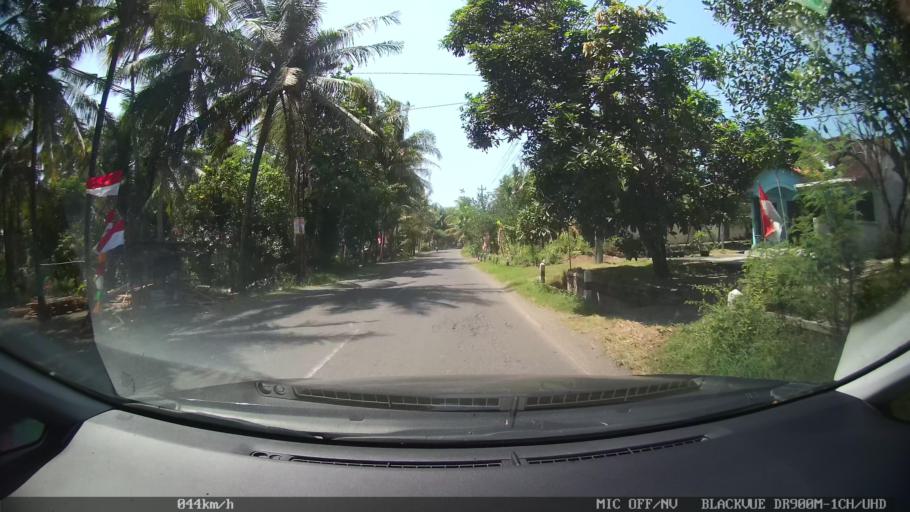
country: ID
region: Daerah Istimewa Yogyakarta
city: Srandakan
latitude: -7.9255
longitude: 110.1238
